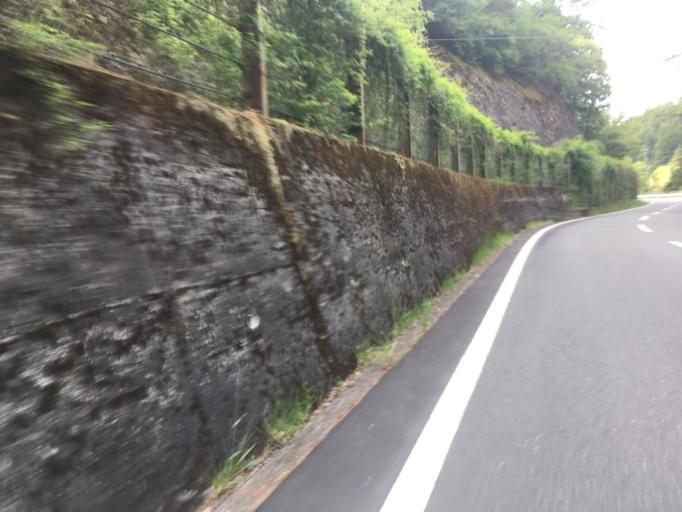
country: JP
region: Kyoto
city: Kameoka
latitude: 35.0947
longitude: 135.6044
